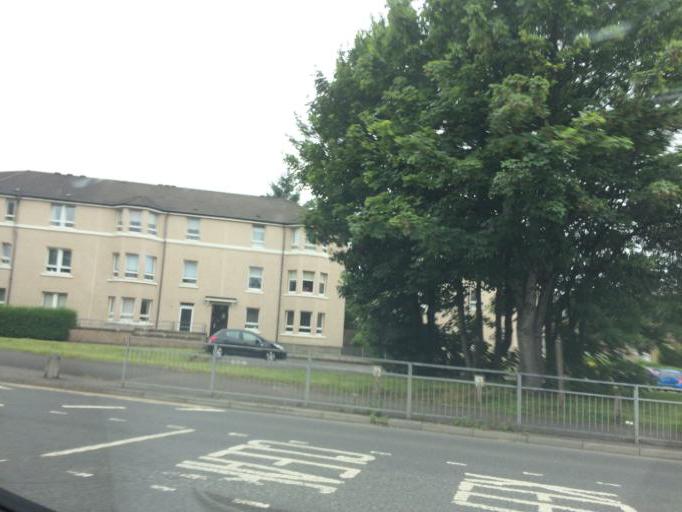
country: GB
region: Scotland
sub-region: East Renfrewshire
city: Giffnock
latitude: 55.8484
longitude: -4.3196
